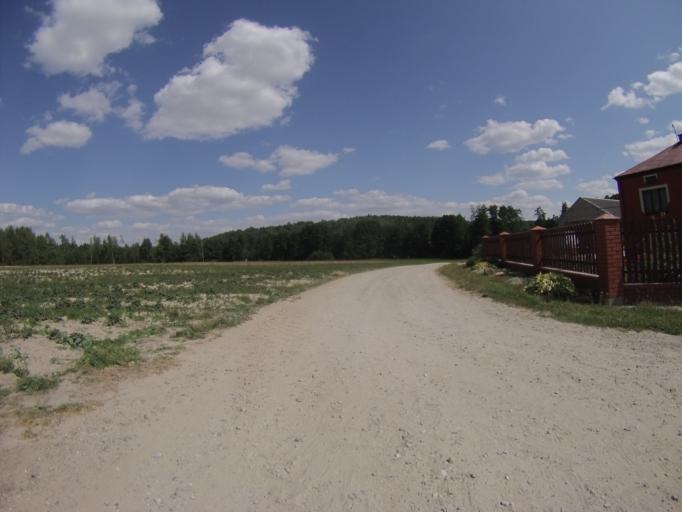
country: PL
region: Swietokrzyskie
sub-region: Powiat kielecki
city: Rakow
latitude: 50.7158
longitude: 21.0468
